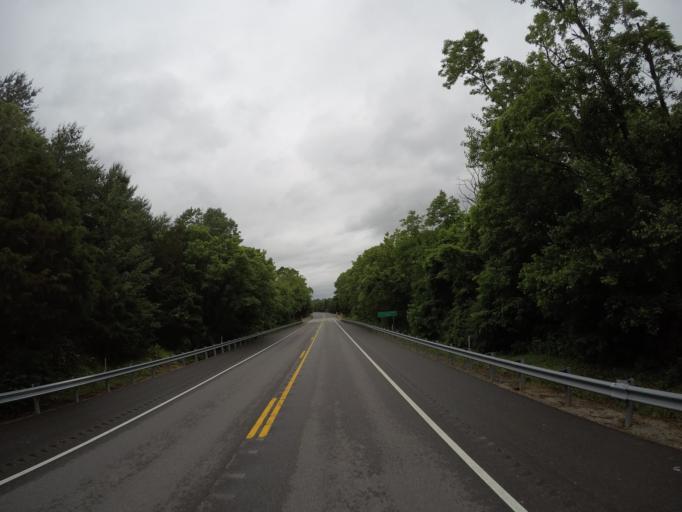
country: US
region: Maryland
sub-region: Washington County
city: Keedysville
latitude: 39.4848
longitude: -77.7045
